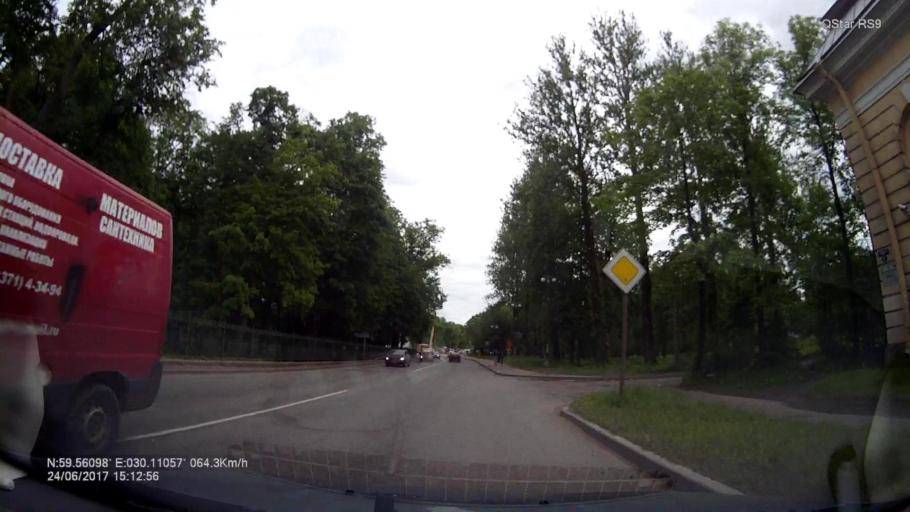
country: RU
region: Leningrad
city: Gatchina
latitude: 59.5608
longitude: 30.1108
